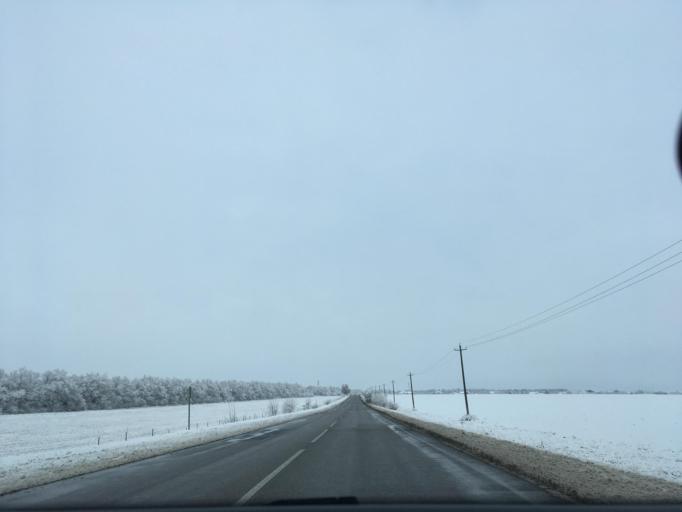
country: RU
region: Voronezj
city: Ol'khovatka
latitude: 50.0254
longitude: 39.0659
